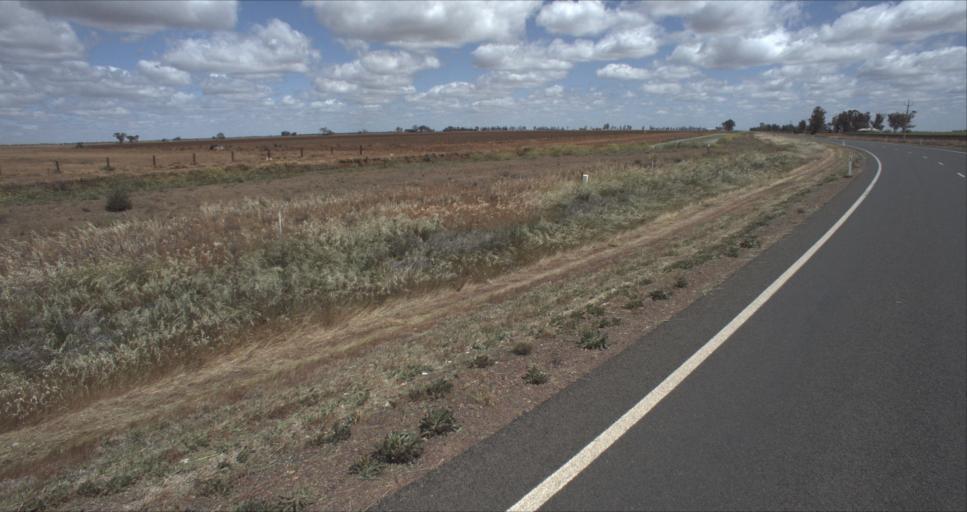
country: AU
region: New South Wales
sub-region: Murrumbidgee Shire
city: Darlington Point
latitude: -34.4758
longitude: 146.1490
